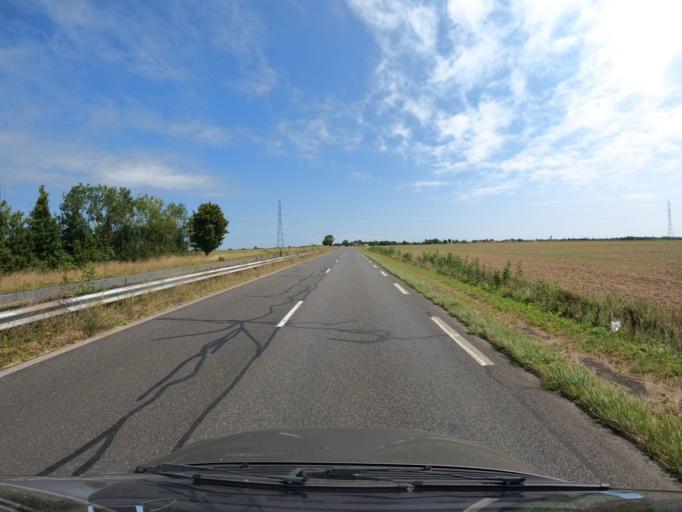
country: FR
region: Poitou-Charentes
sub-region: Departement des Deux-Sevres
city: Frontenay-Rohan-Rohan
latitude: 46.2499
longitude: -0.5568
